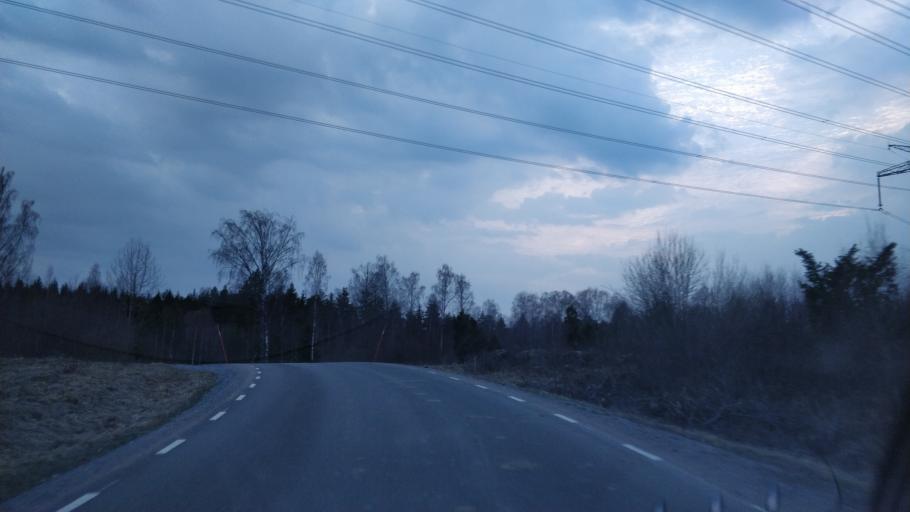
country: SE
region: Uppsala
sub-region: Enkopings Kommun
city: Orsundsbro
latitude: 59.7255
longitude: 17.2827
